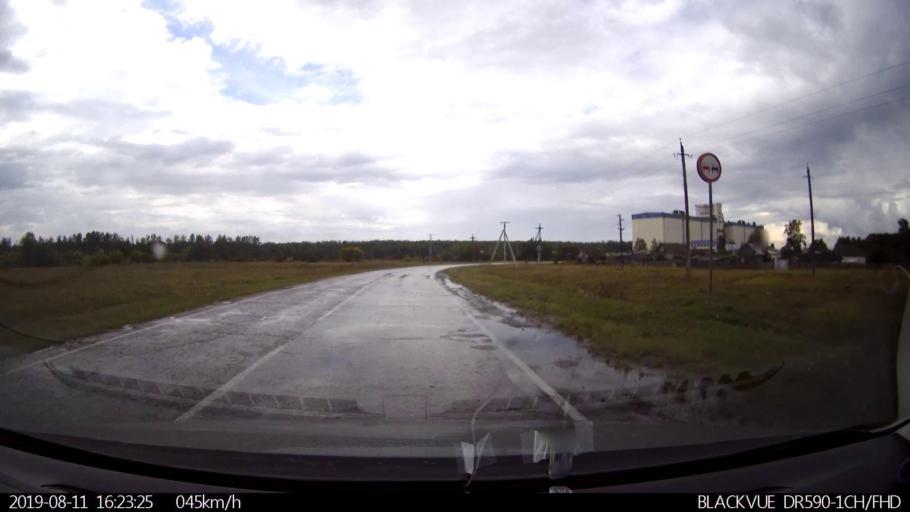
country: RU
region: Ulyanovsk
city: Mayna
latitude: 54.0949
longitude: 47.5886
